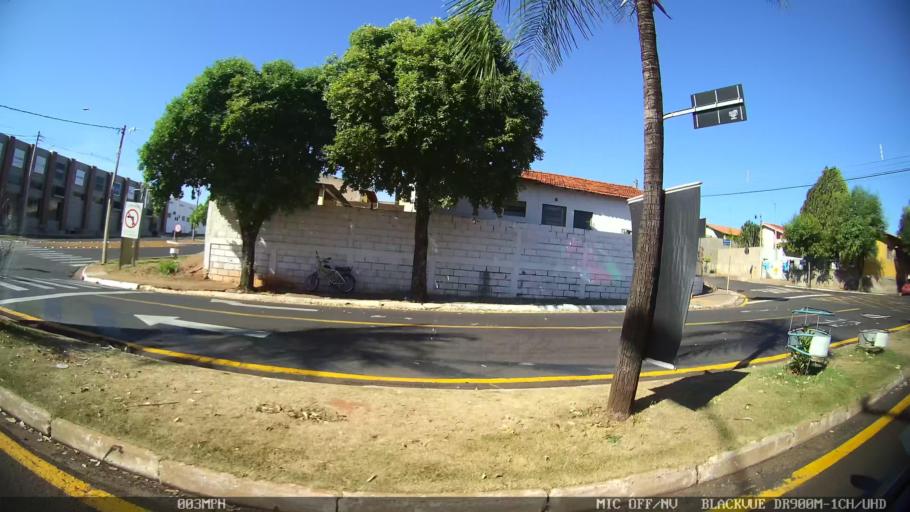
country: BR
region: Sao Paulo
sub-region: Olimpia
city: Olimpia
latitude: -20.7399
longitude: -48.9033
